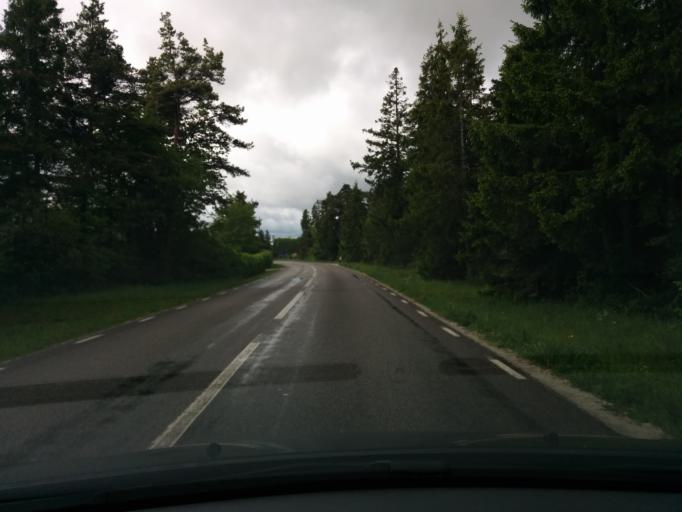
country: SE
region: Gotland
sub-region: Gotland
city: Slite
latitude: 57.5903
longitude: 18.7310
